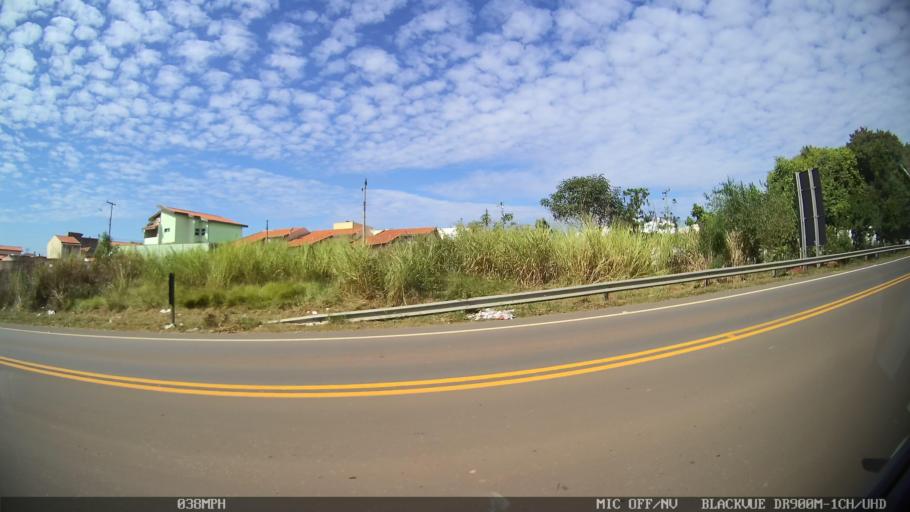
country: BR
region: Sao Paulo
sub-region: Santa Barbara D'Oeste
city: Santa Barbara d'Oeste
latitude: -22.7401
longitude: -47.4247
